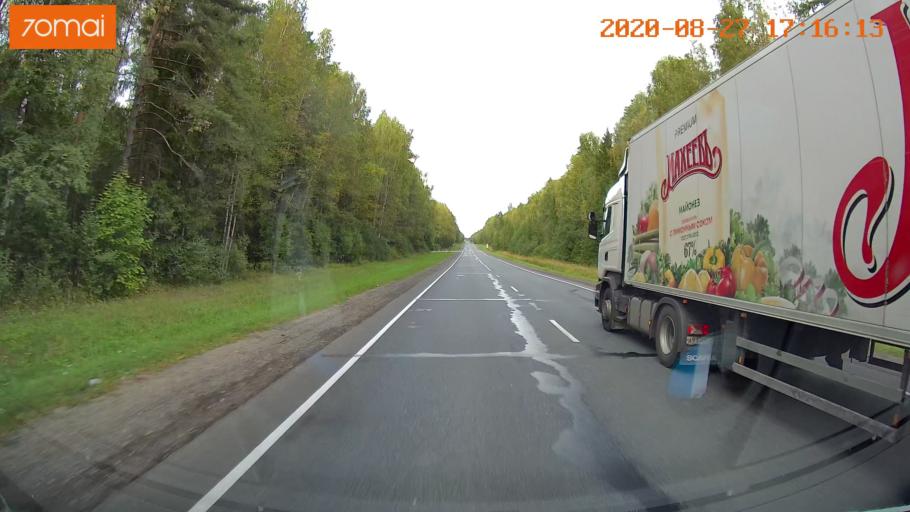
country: RU
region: Ivanovo
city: Lezhnevo
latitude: 56.7459
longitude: 40.7456
